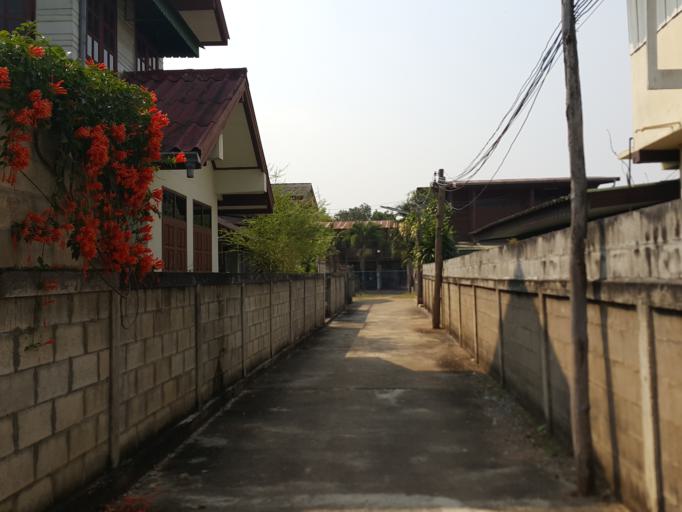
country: TH
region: Sukhothai
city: Thung Saliam
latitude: 17.3265
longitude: 99.5329
